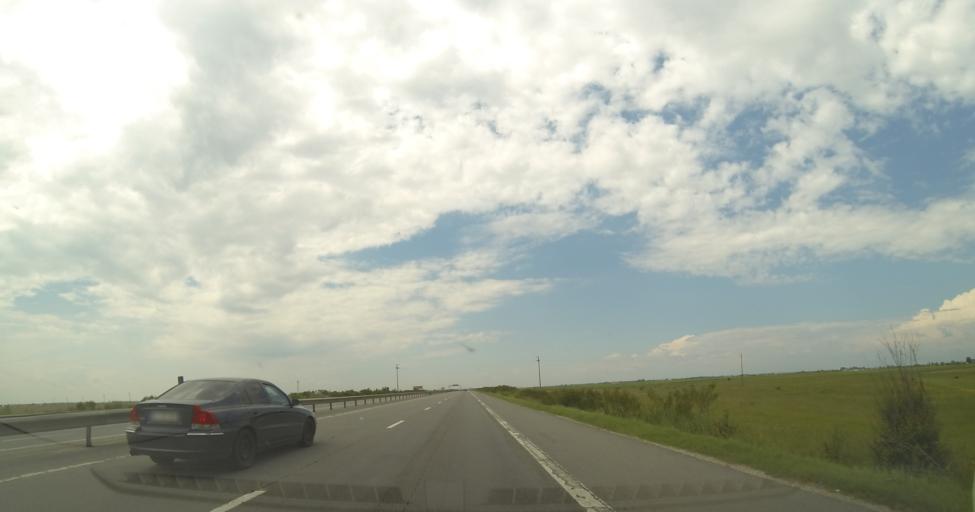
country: RO
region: Dambovita
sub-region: Comuna Petresti
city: Petresti
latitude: 44.6591
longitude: 25.3322
